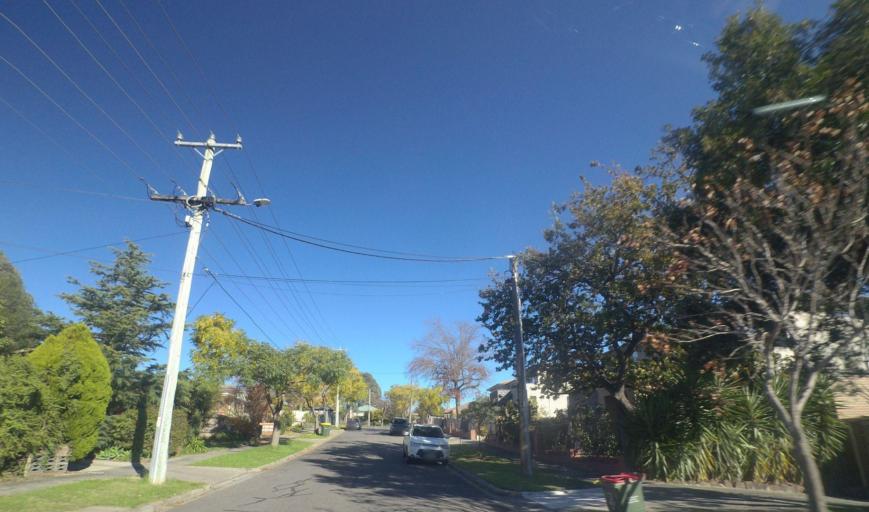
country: AU
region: Victoria
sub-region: Whitehorse
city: Blackburn North
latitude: -37.8097
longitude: 145.1388
